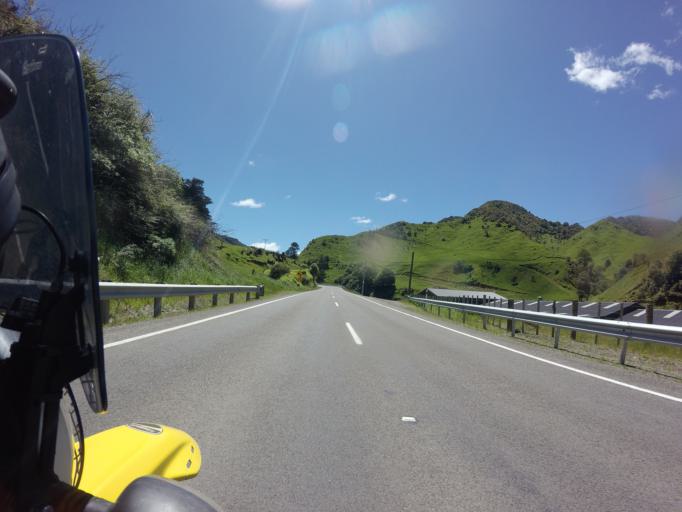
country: NZ
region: Bay of Plenty
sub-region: Opotiki District
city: Opotiki
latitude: -38.3790
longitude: 177.4694
